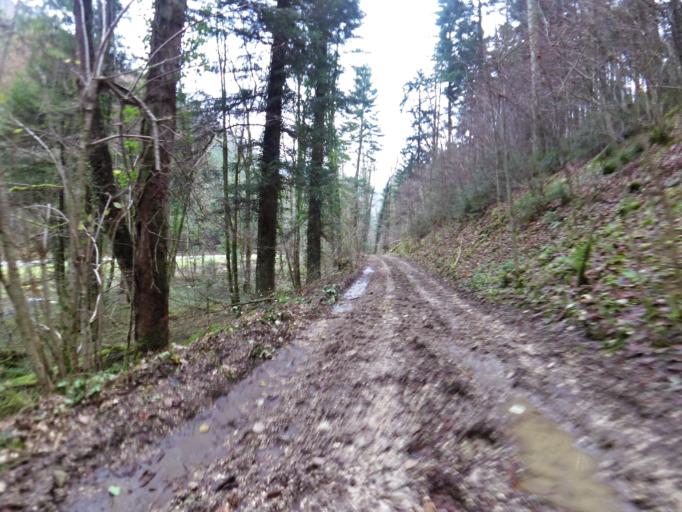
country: FR
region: Alsace
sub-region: Departement du Haut-Rhin
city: Ferrette
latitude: 47.4347
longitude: 7.2829
